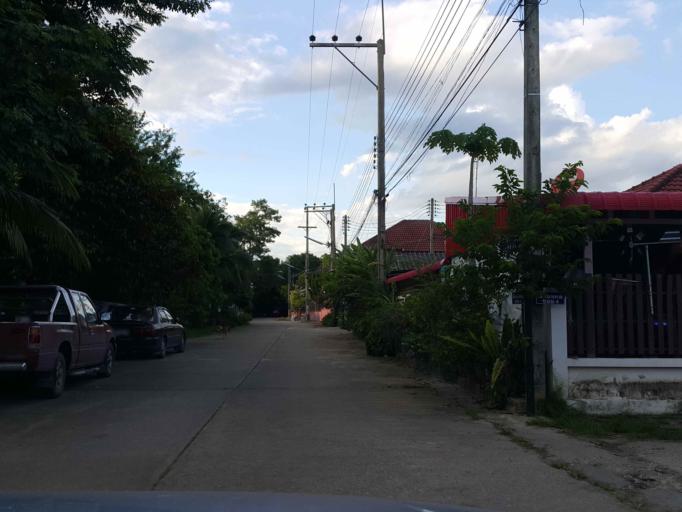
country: TH
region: Chiang Mai
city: San Sai
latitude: 18.9251
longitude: 98.9785
